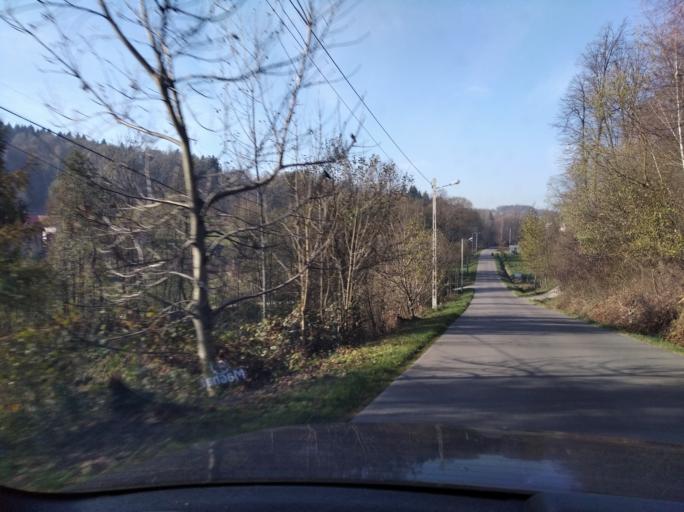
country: PL
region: Subcarpathian Voivodeship
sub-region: Powiat strzyzowski
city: Wisniowa
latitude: 49.8752
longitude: 21.6210
